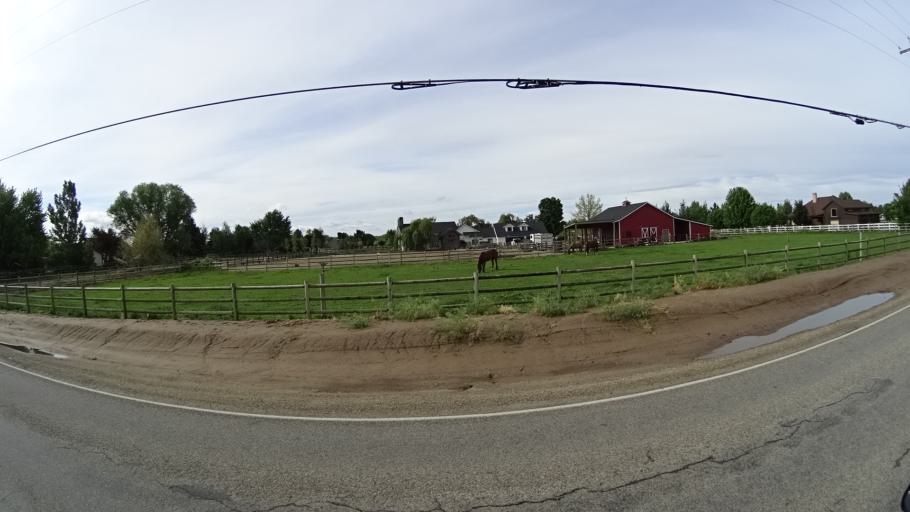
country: US
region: Idaho
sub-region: Ada County
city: Eagle
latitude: 43.7208
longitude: -116.3658
